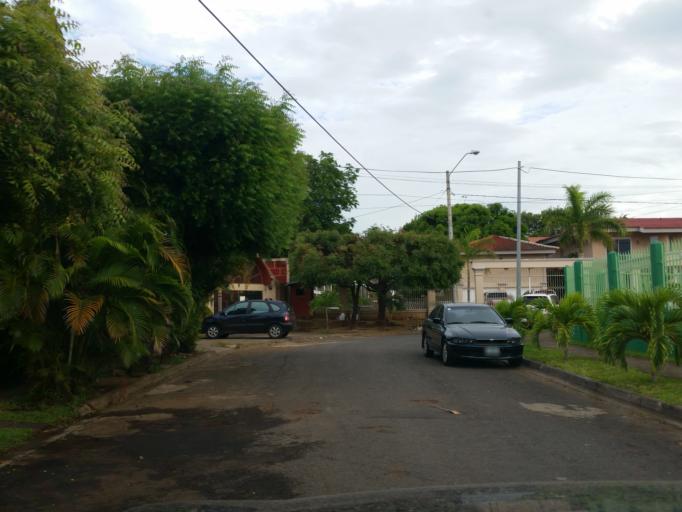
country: NI
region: Managua
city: Managua
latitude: 12.1068
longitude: -86.2603
